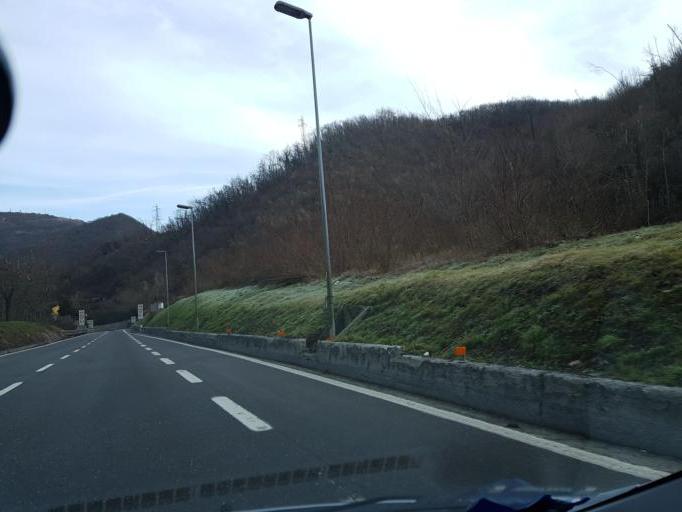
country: IT
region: Liguria
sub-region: Provincia di Genova
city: Isola del Cantone
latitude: 44.6400
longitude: 8.9549
